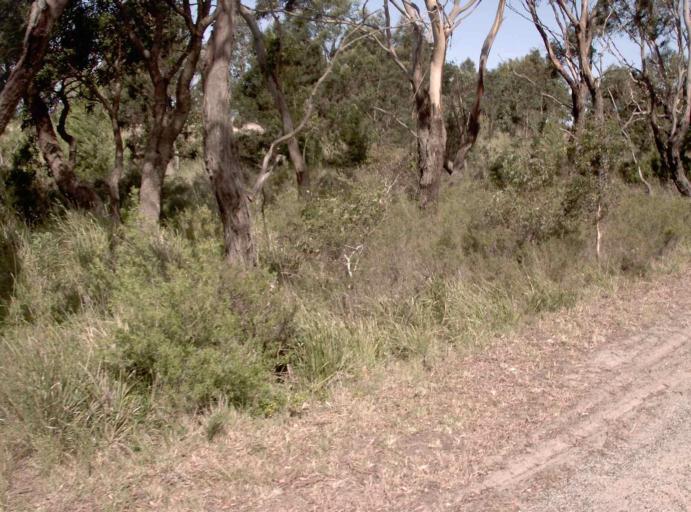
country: AU
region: Victoria
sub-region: Wellington
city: Sale
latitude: -38.3263
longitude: 147.1614
